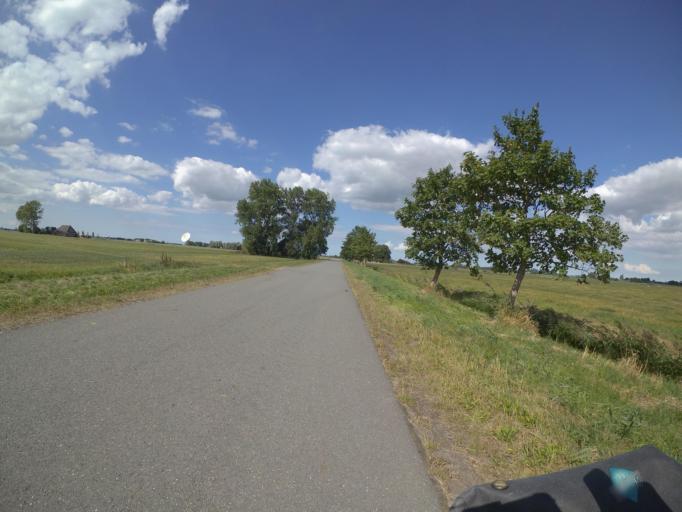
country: NL
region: Friesland
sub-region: Gemeente Kollumerland en Nieuwkruisland
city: Kollum
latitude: 53.2763
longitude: 6.2237
